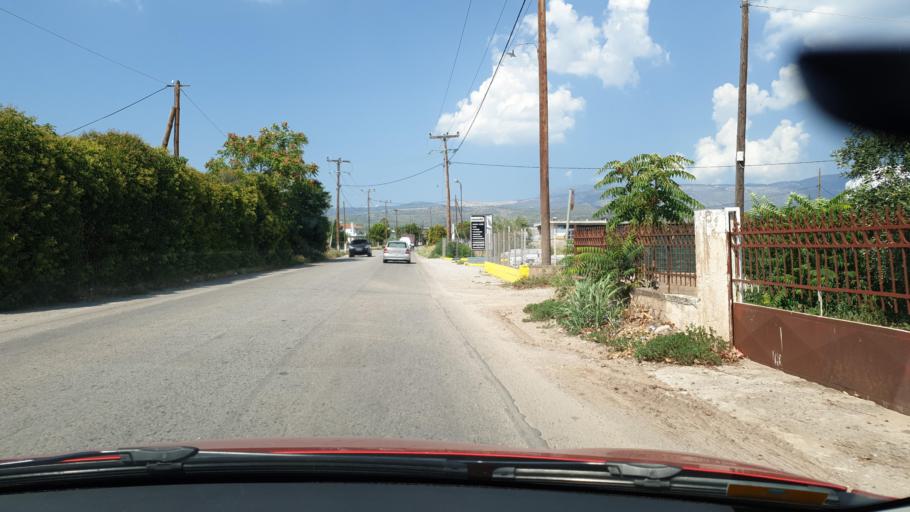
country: GR
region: Central Greece
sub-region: Nomos Evvoias
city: Kastella
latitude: 38.5638
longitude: 23.6313
